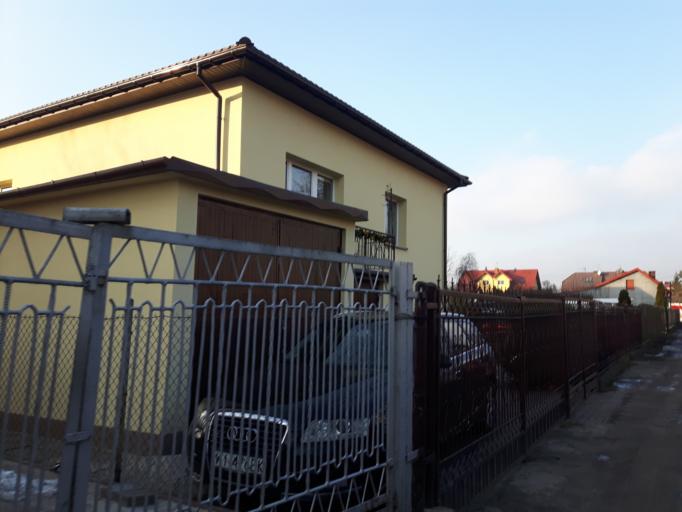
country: PL
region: Masovian Voivodeship
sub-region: Powiat wolominski
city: Zabki
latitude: 52.2889
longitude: 21.1024
